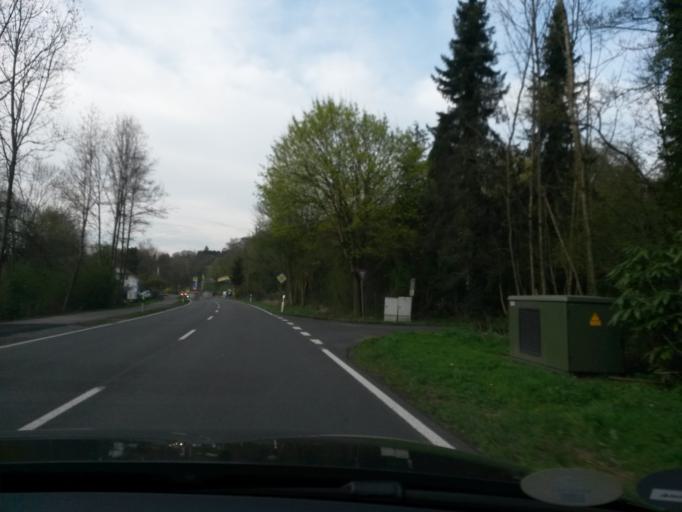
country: DE
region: North Rhine-Westphalia
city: Lohmar
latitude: 50.8684
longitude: 7.2514
